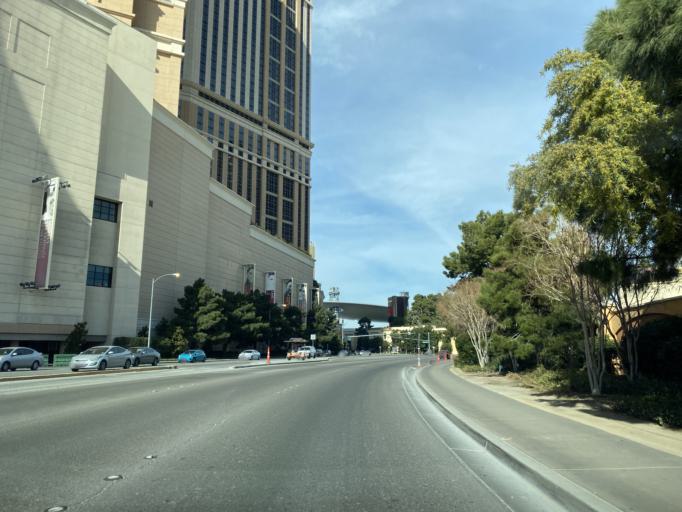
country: US
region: Nevada
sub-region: Clark County
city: Paradise
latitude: 36.1231
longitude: -115.1660
